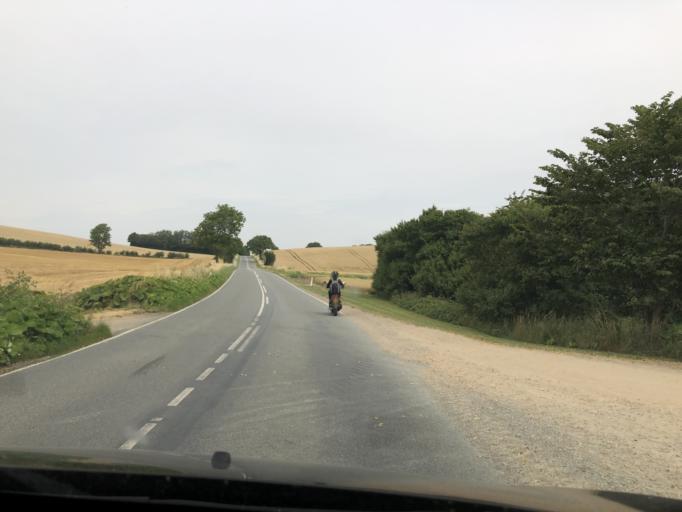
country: DK
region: South Denmark
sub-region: Assens Kommune
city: Arup
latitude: 55.3130
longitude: 10.0500
